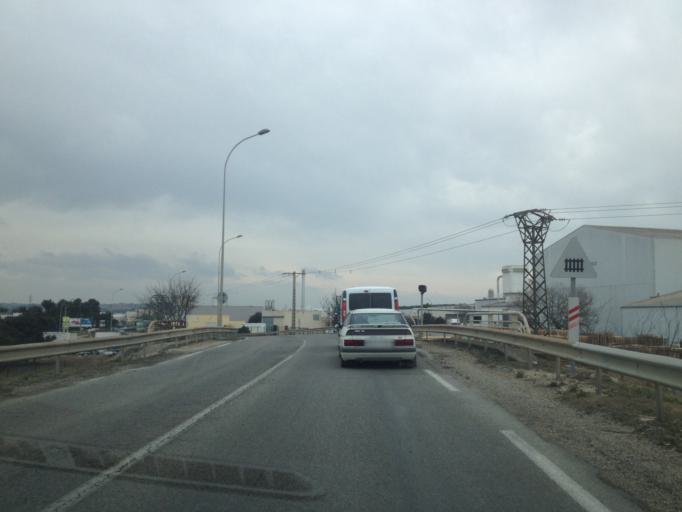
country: FR
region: Provence-Alpes-Cote d'Azur
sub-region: Departement du Vaucluse
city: Sorgues
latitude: 44.0095
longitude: 4.8877
